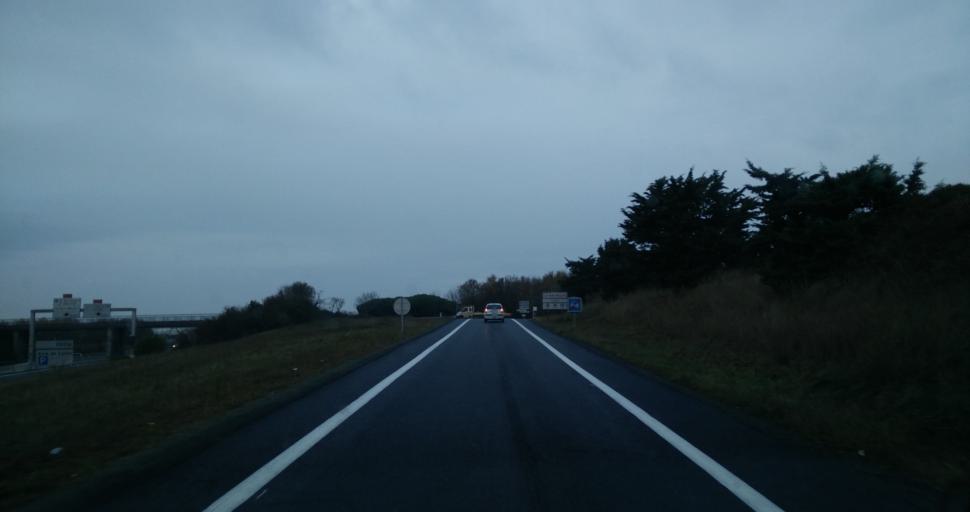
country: FR
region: Poitou-Charentes
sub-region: Departement de la Charente-Maritime
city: Lagord
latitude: 46.1728
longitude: -1.1975
